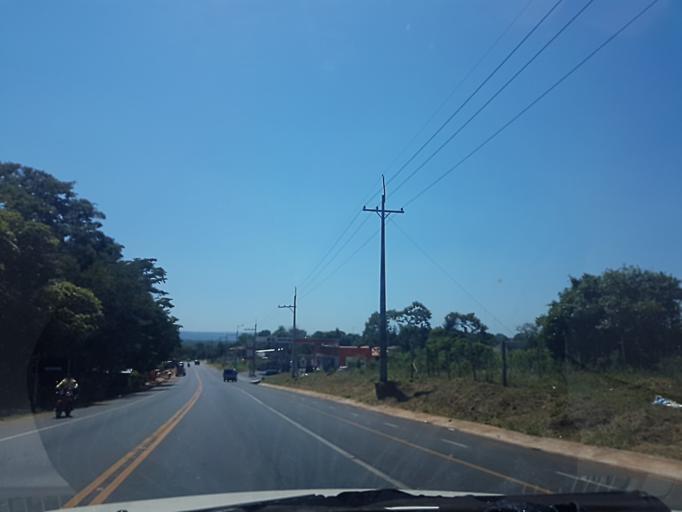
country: PY
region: Central
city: Aregua
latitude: -25.2391
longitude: -57.4311
